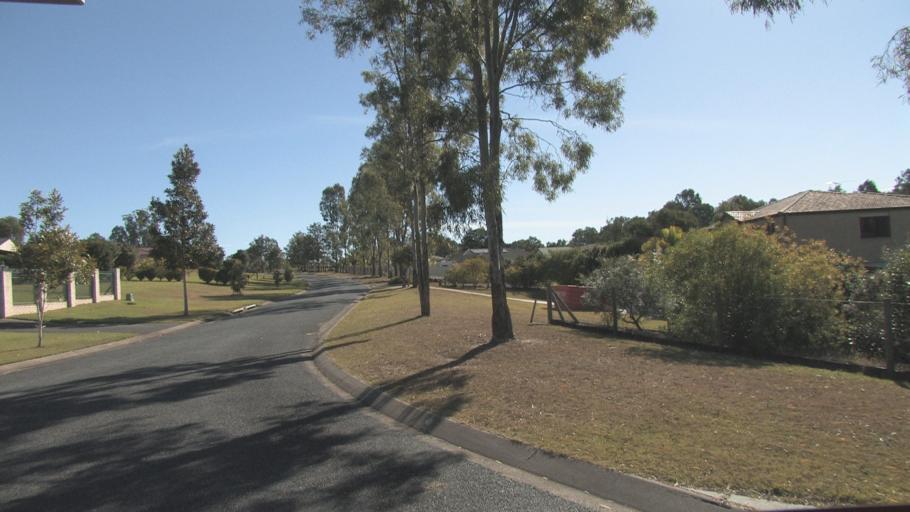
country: AU
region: Queensland
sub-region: Ipswich
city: Springfield Lakes
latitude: -27.7291
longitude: 152.9455
